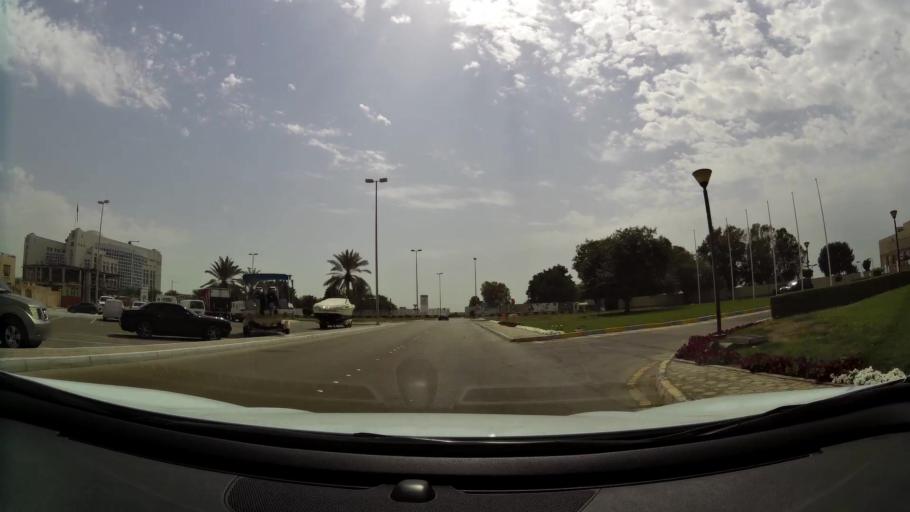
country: AE
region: Abu Dhabi
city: Abu Dhabi
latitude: 24.4568
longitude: 54.3300
